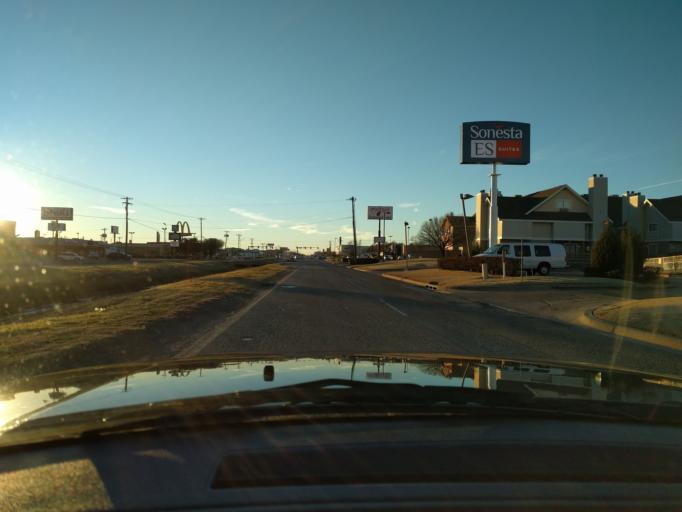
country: US
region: Oklahoma
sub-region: Oklahoma County
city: Warr Acres
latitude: 35.4644
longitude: -97.5981
